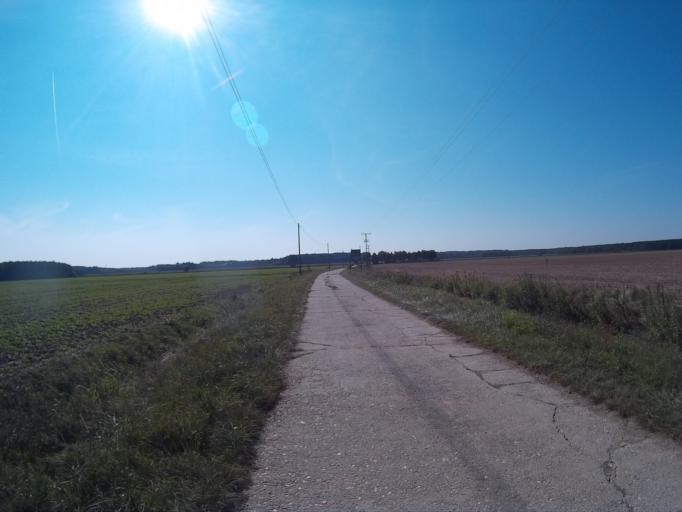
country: HU
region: Vas
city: Kormend
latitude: 47.0773
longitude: 16.6292
